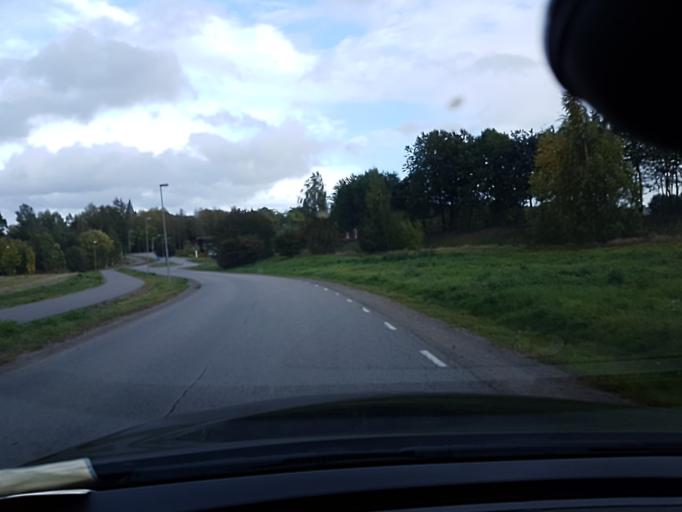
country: SE
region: Kronoberg
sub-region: Vaxjo Kommun
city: Vaexjoe
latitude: 56.8580
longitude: 14.8265
